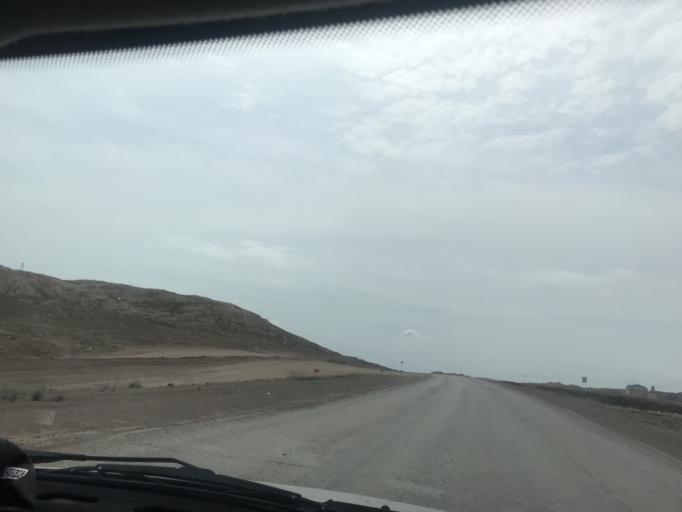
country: KZ
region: Zhambyl
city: Mynaral
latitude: 45.3708
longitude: 73.6583
